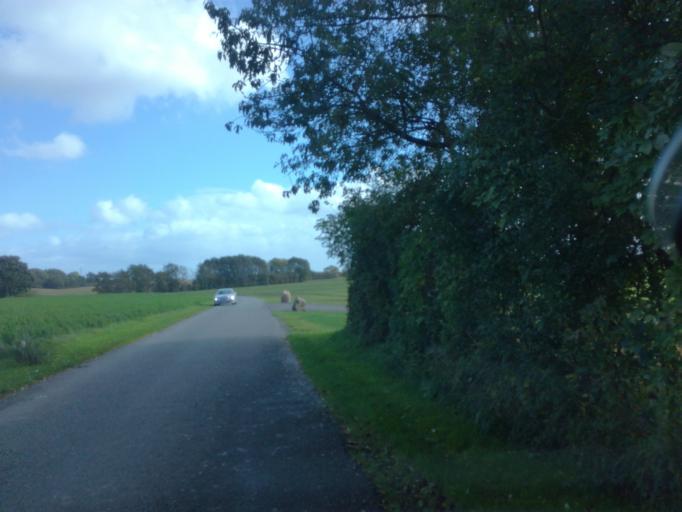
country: DK
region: South Denmark
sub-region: Fredericia Kommune
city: Fredericia
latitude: 55.6107
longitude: 9.7316
